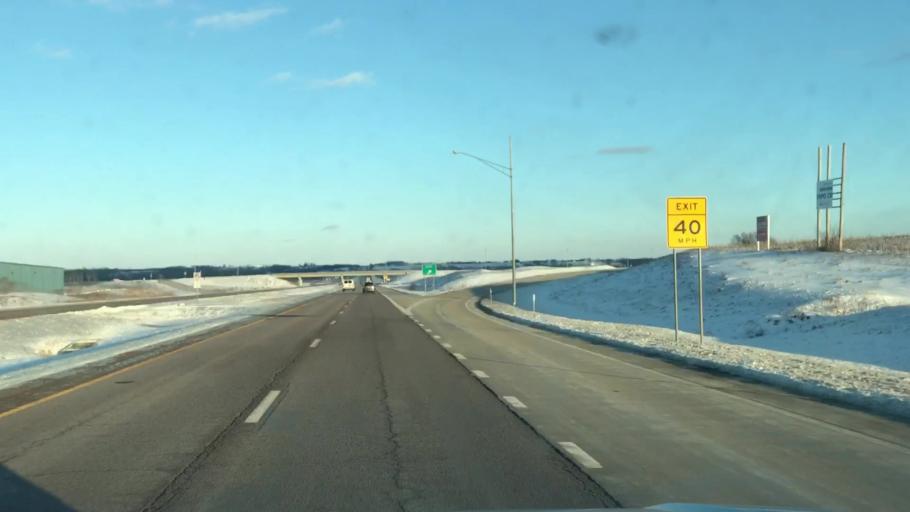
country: US
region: Missouri
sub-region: Buchanan County
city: Saint Joseph
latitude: 39.7480
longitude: -94.7559
